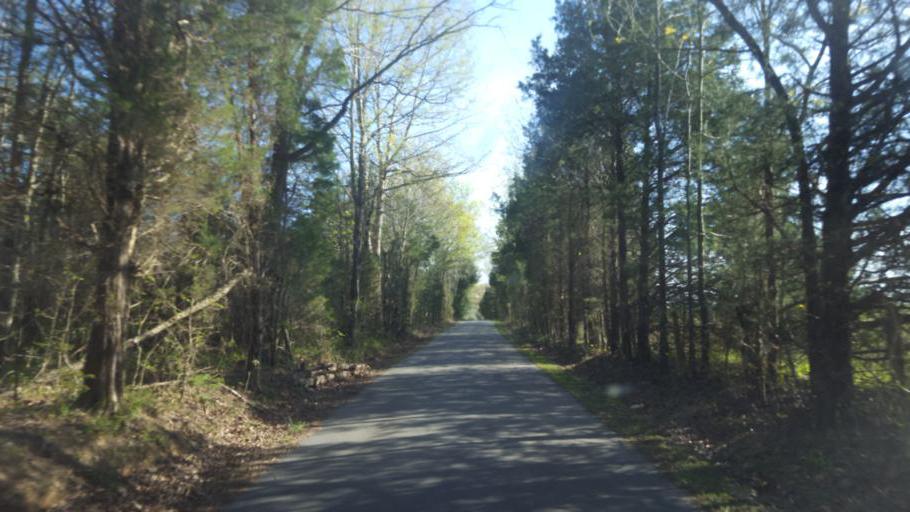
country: US
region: Kentucky
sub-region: Barren County
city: Cave City
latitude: 37.1784
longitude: -85.9968
